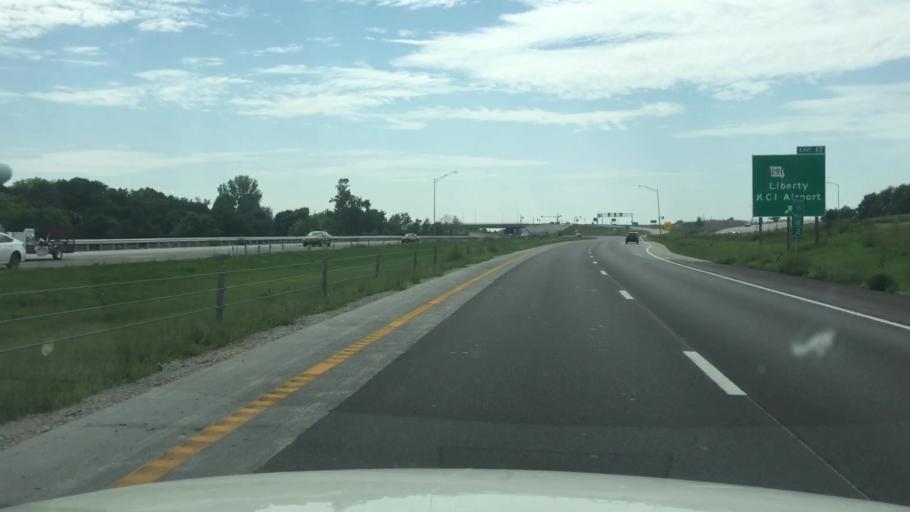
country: US
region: Missouri
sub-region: Clay County
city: Liberty
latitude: 39.2682
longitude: -94.4401
